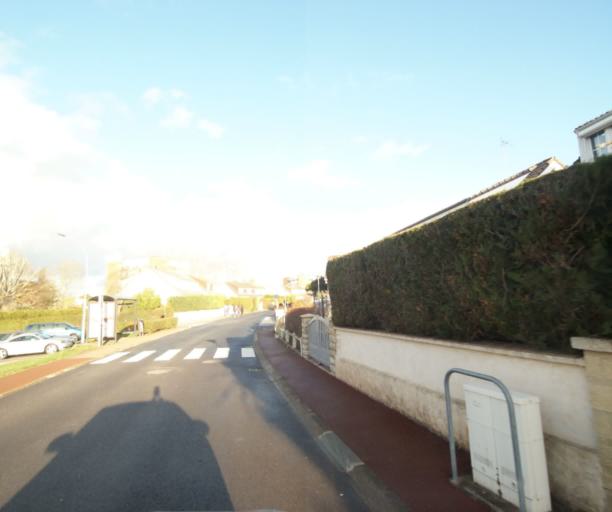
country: FR
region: Ile-de-France
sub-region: Departement des Yvelines
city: Meulan-en-Yvelines
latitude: 49.0109
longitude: 1.9190
